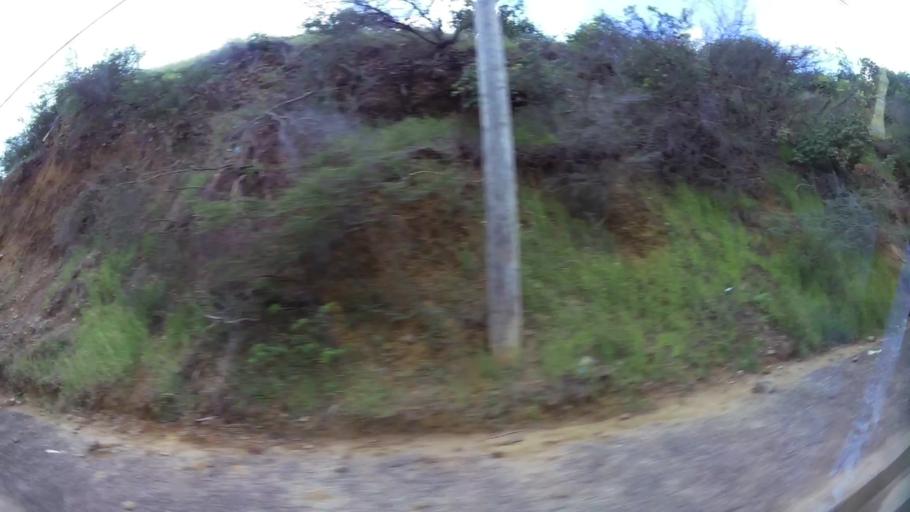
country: MS
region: Saint Peter
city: Brades
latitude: 16.7986
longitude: -62.2038
